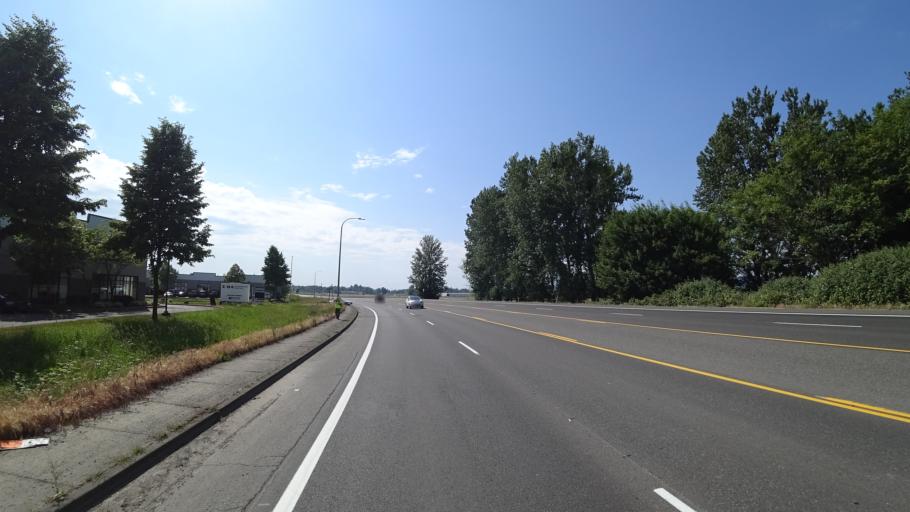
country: US
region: Oregon
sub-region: Multnomah County
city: Troutdale
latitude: 45.5477
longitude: -122.4036
